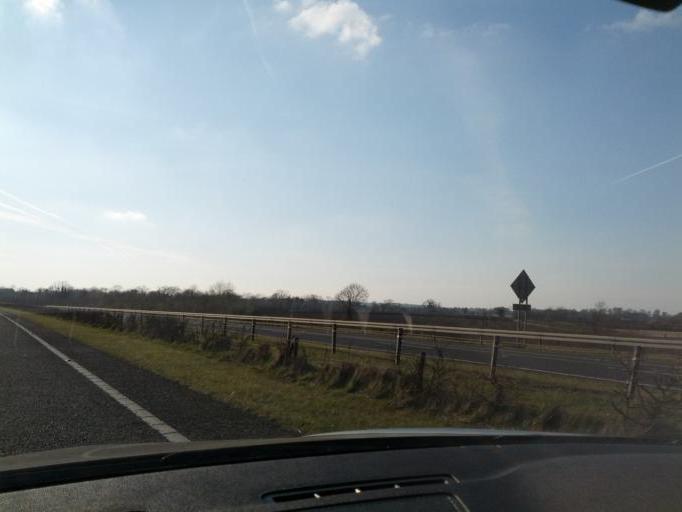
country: IE
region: Leinster
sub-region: Kildare
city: Monasterevin
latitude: 53.1141
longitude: -7.0896
